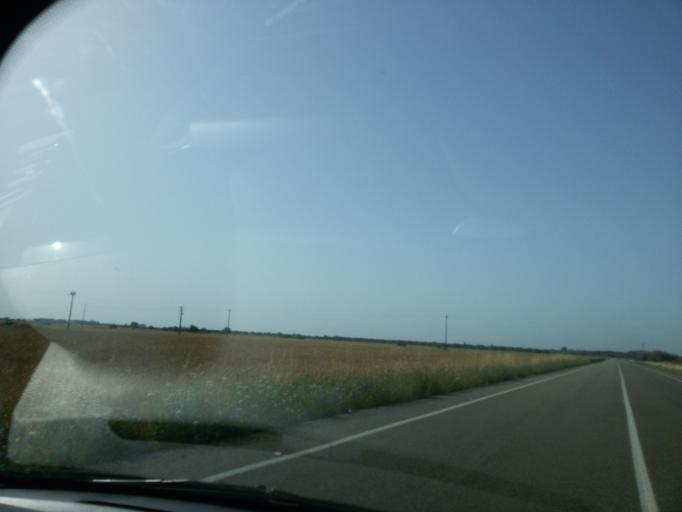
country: IT
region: Apulia
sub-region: Provincia di Brindisi
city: Mesagne
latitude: 40.5027
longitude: 17.8282
